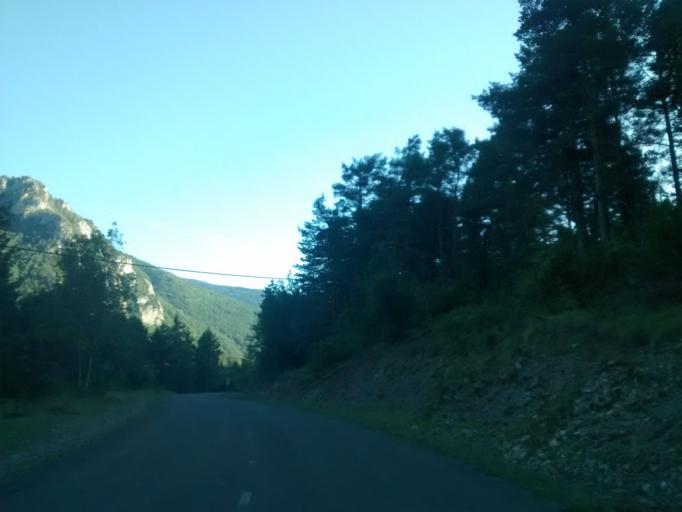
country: ES
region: Aragon
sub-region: Provincia de Huesca
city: Anso
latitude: 42.7936
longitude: -0.7363
